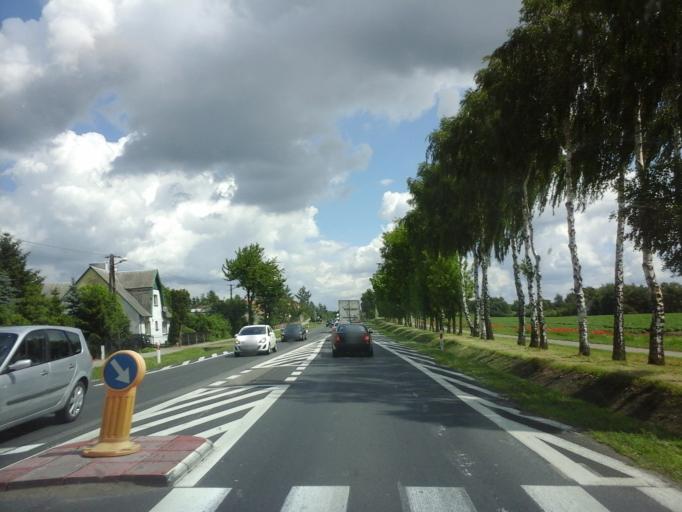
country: PL
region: West Pomeranian Voivodeship
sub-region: Powiat koszalinski
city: Mielno
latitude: 54.1369
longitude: 16.0473
